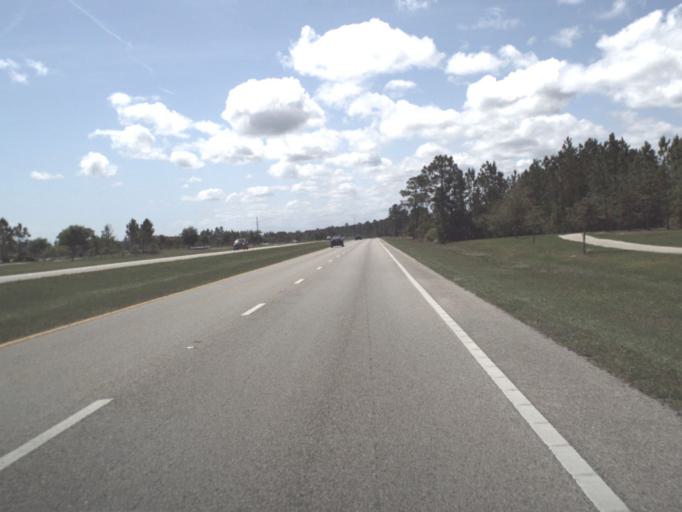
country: US
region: Florida
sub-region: Flagler County
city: Palm Coast
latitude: 29.5853
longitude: -81.2793
